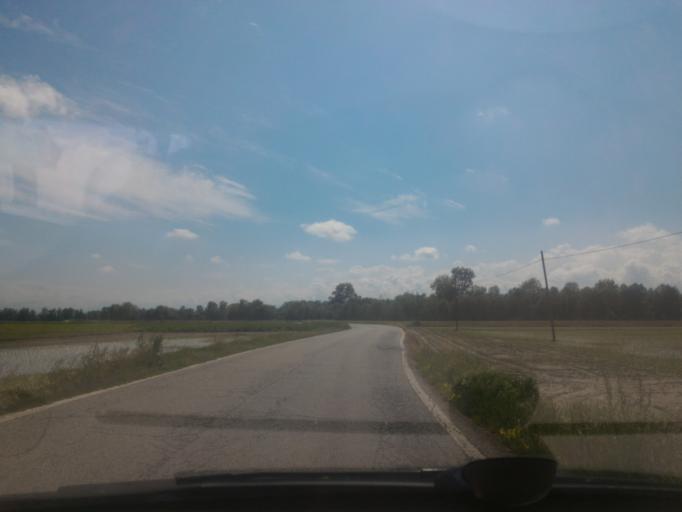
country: IT
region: Piedmont
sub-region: Provincia di Torino
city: Pancalieri
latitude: 44.8205
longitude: 7.5865
